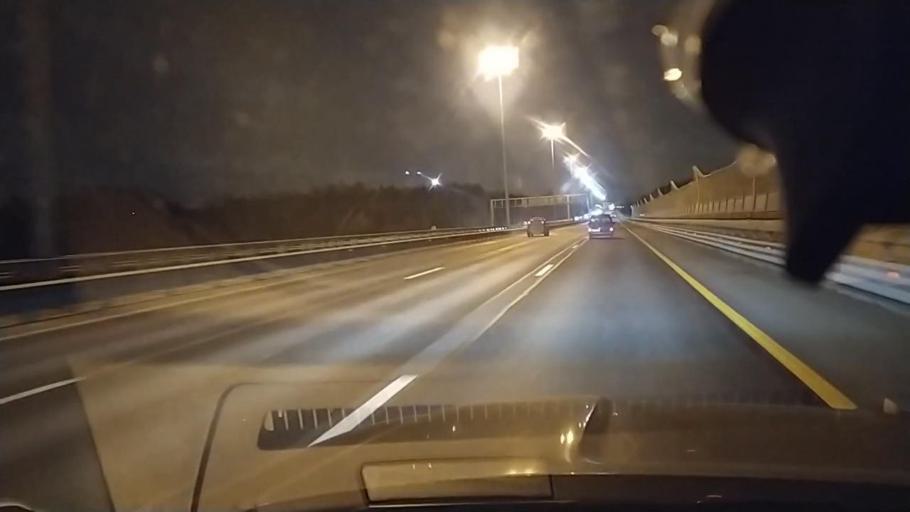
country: RU
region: Leningrad
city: Untolovo
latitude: 60.0347
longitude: 30.1863
